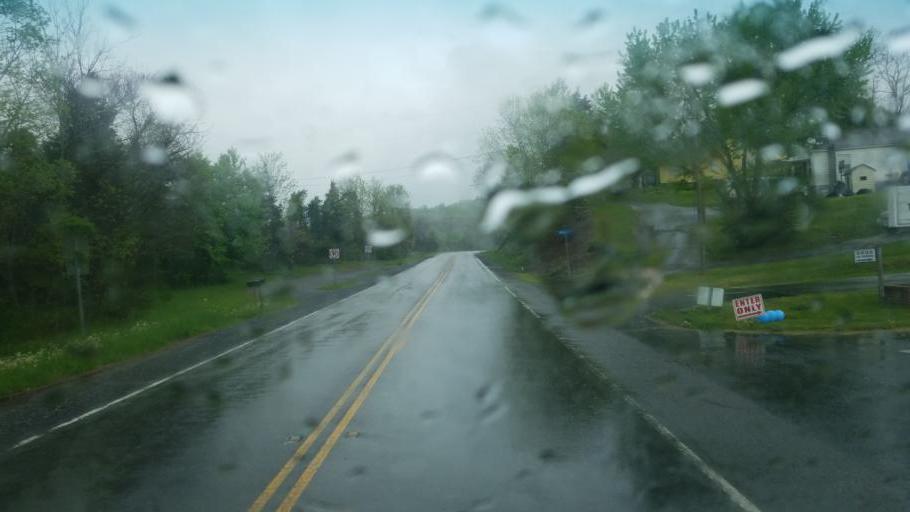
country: US
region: Virginia
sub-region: Smyth County
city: Adwolf
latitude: 36.8163
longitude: -81.5620
